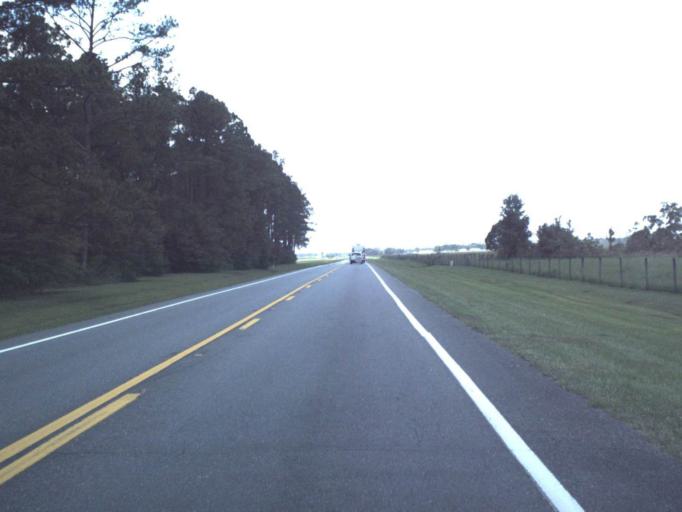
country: US
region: Florida
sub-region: Bradford County
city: Starke
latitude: 30.0420
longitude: -82.1671
